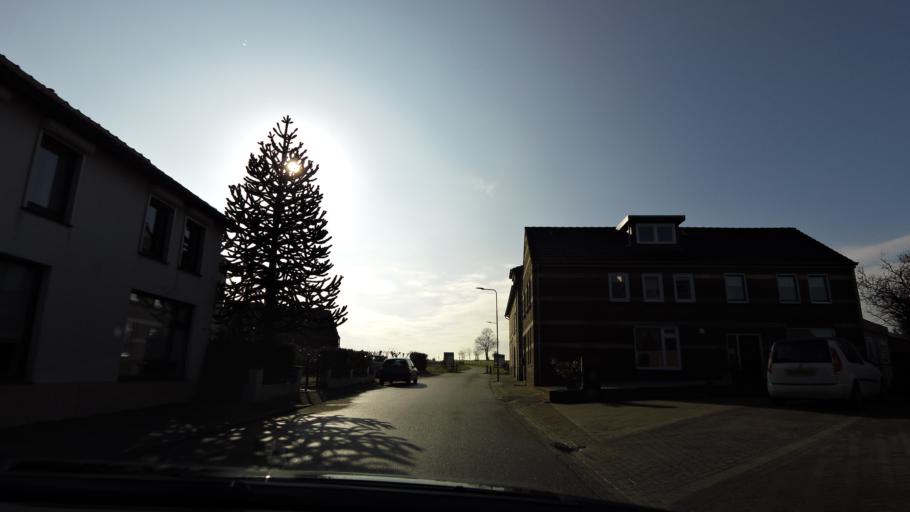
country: NL
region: Limburg
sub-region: Valkenburg aan de Geul
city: Sibbe
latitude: 50.8380
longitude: 5.8341
